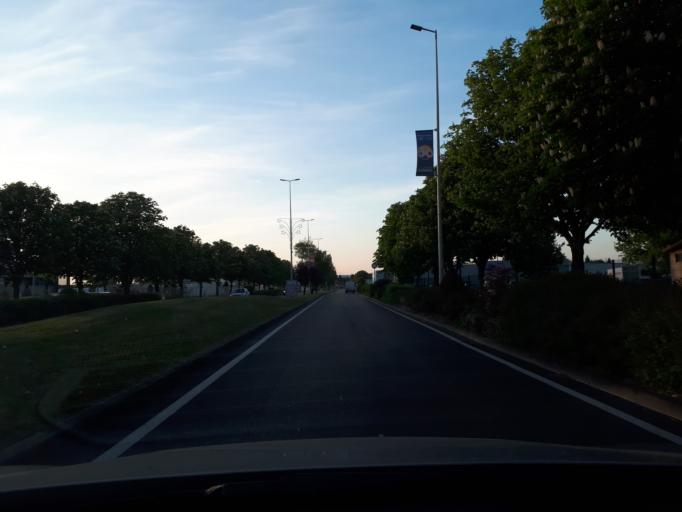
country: FR
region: Rhone-Alpes
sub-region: Departement de l'Isere
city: Bourgoin-Jallieu
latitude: 45.5945
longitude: 5.2698
